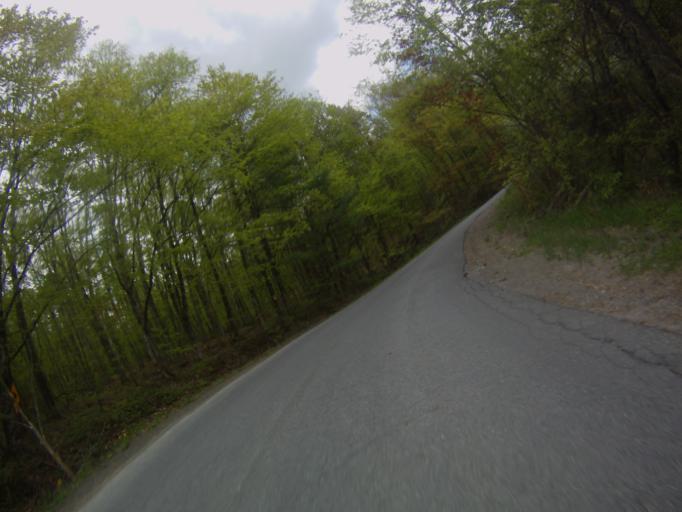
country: US
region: New York
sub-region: Essex County
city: Ticonderoga
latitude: 43.8822
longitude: -73.4787
